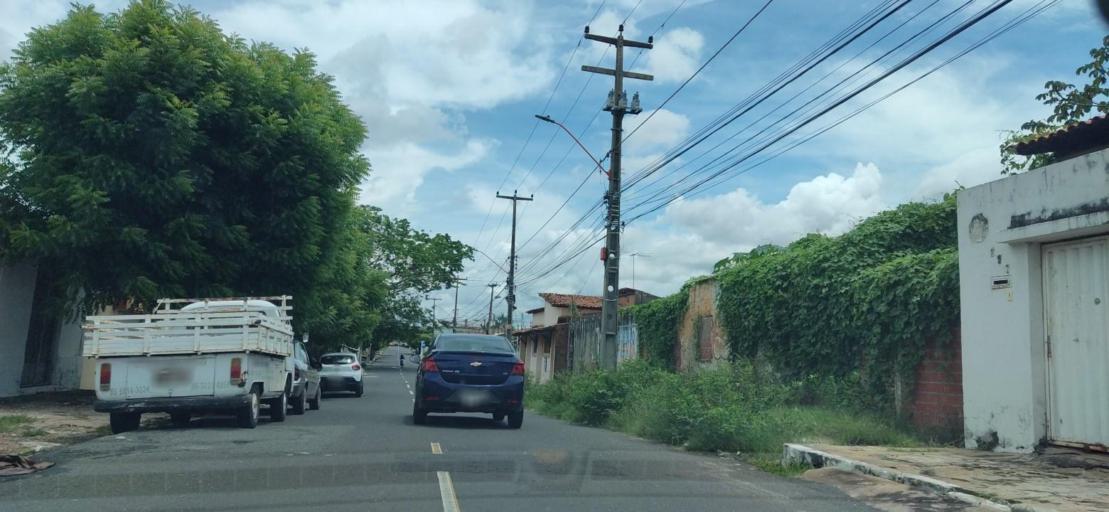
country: BR
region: Piaui
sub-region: Teresina
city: Teresina
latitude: -5.0750
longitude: -42.8051
